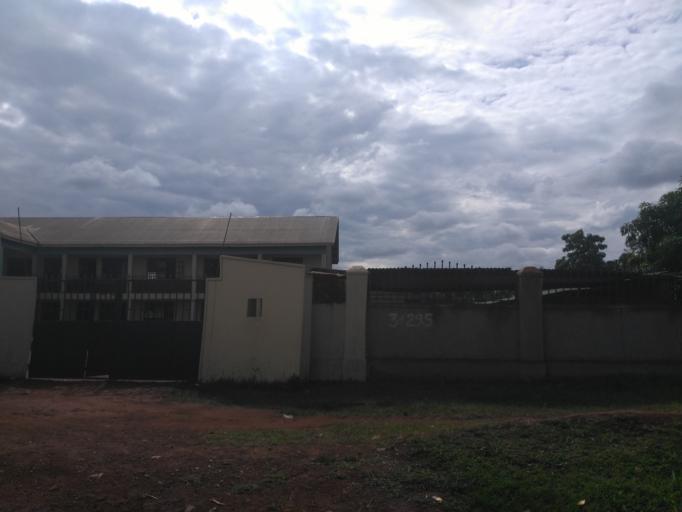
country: UG
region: Central Region
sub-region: Buikwe District
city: Njeru
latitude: 0.3929
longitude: 33.1708
